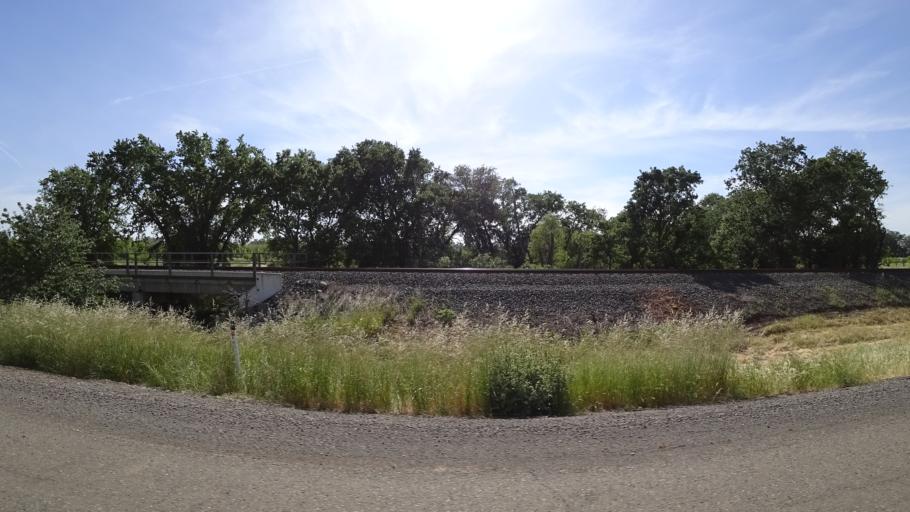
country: US
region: California
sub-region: Tehama County
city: Los Molinos
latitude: 39.9818
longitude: -122.0799
